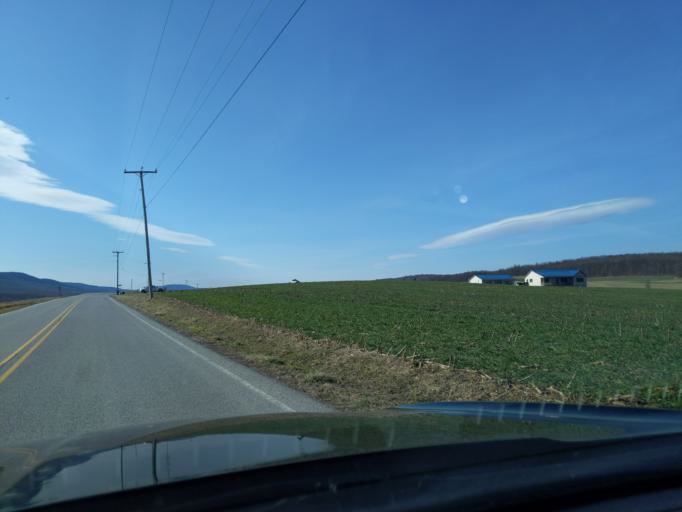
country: US
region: Pennsylvania
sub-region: Blair County
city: Martinsburg
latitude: 40.3567
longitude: -78.2508
